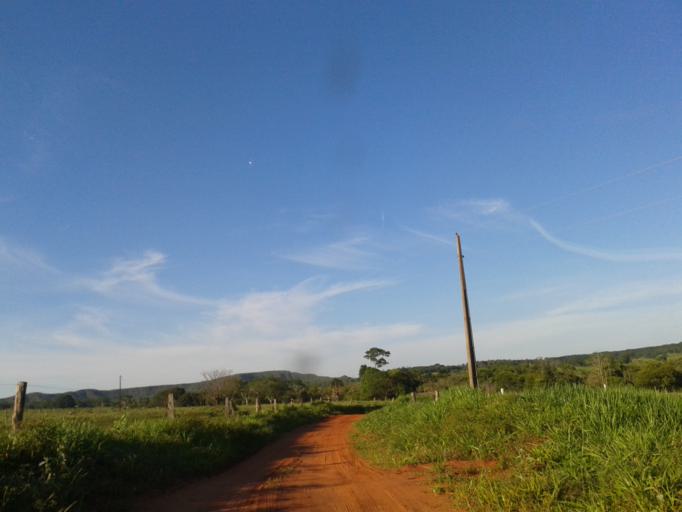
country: BR
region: Minas Gerais
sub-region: Santa Vitoria
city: Santa Vitoria
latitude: -18.9609
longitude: -49.8665
